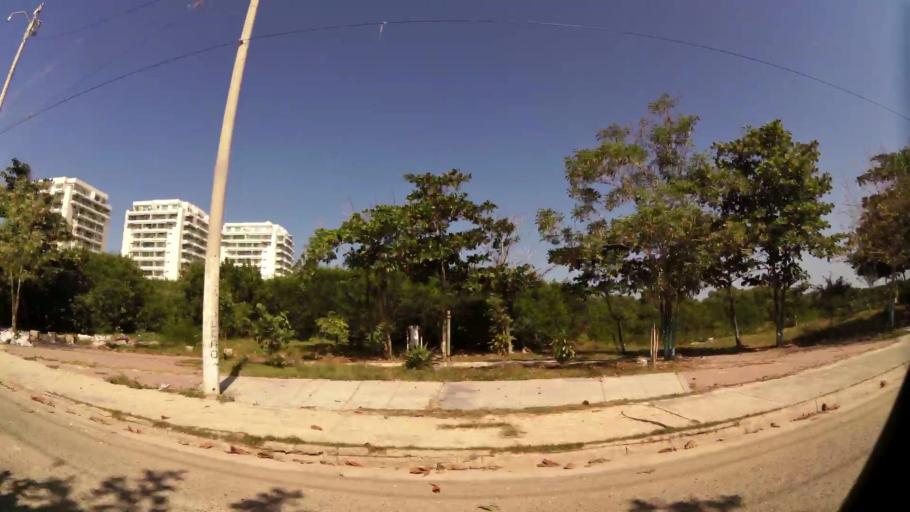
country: CO
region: Bolivar
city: Cartagena
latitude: 10.4373
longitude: -75.5300
